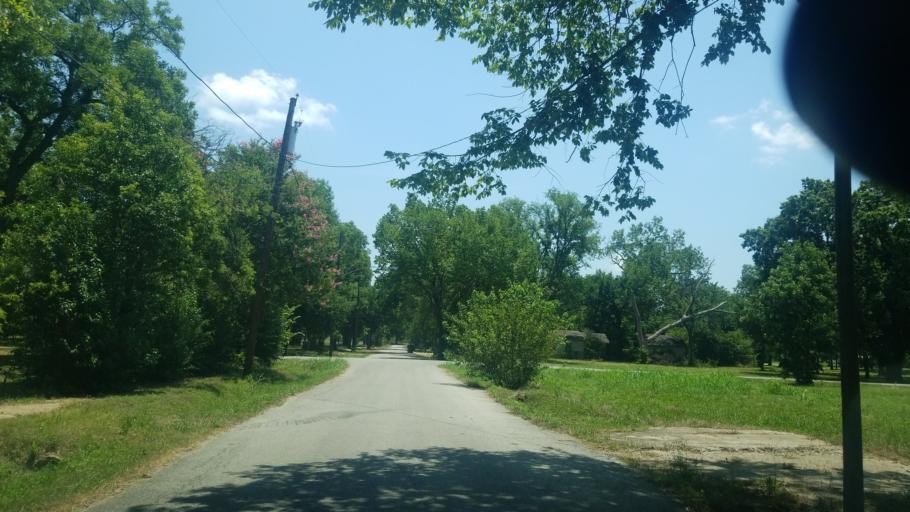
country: US
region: Texas
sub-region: Dallas County
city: Dallas
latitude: 32.7422
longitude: -96.7853
